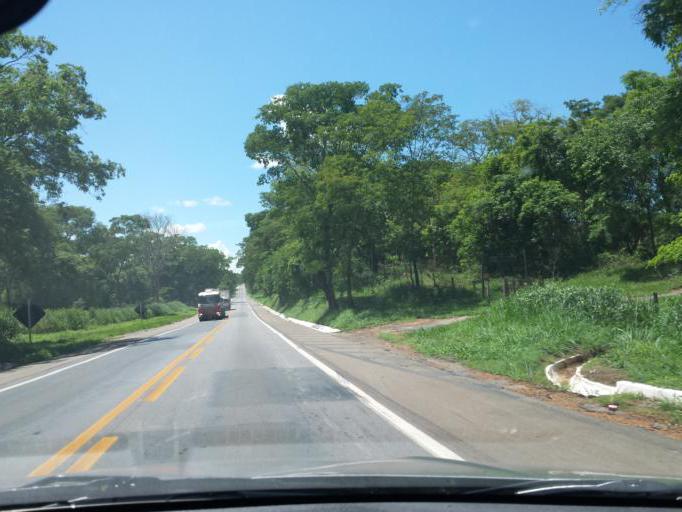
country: BR
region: Goias
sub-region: Luziania
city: Luziania
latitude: -16.3847
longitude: -47.8263
